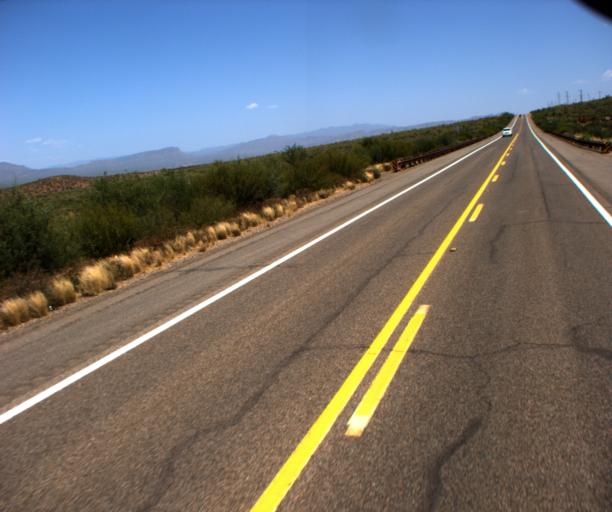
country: US
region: Arizona
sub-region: Gila County
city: Tonto Basin
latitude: 33.6598
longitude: -111.1147
